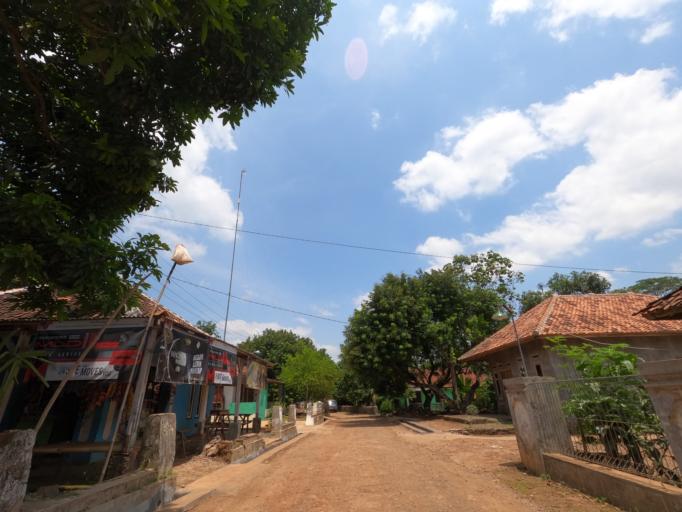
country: ID
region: West Java
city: Pamanukan
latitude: -6.5138
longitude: 107.7725
